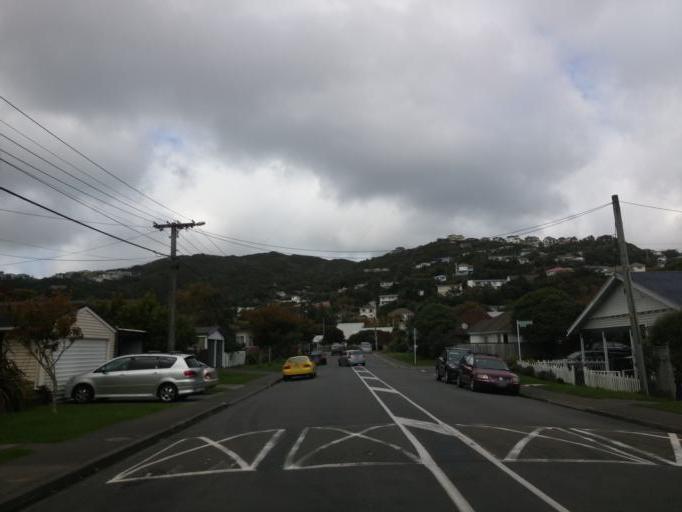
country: NZ
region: Wellington
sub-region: Wellington City
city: Brooklyn
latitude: -41.2849
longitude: 174.7273
